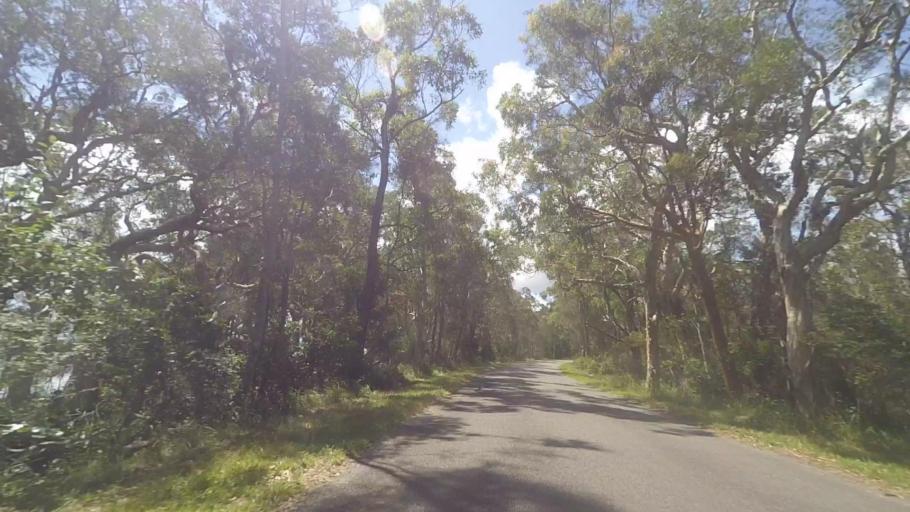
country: AU
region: New South Wales
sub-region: Great Lakes
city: Bulahdelah
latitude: -32.5190
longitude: 152.3222
